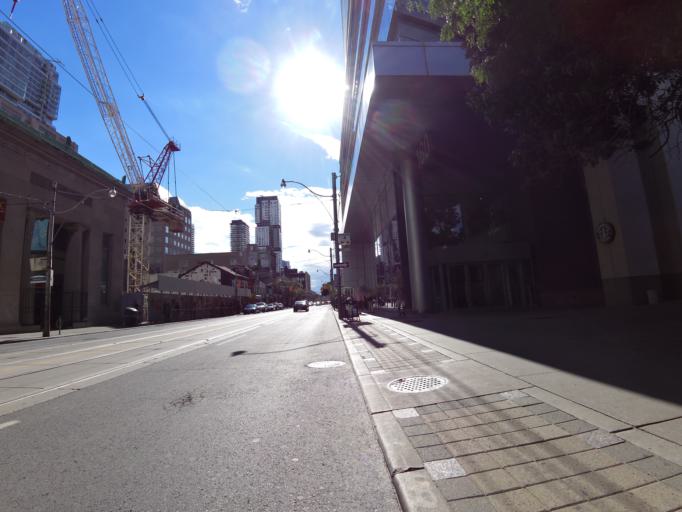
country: CA
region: Ontario
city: Toronto
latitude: 43.6507
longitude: -79.3874
